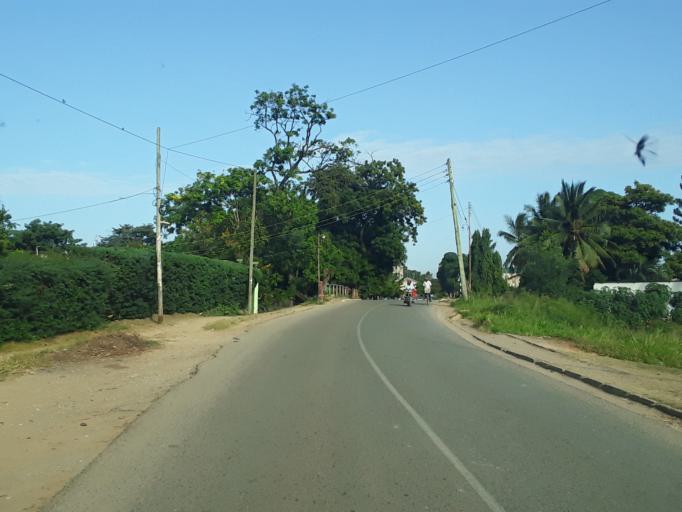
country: TZ
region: Tanga
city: Tanga
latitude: -5.0728
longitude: 39.1086
